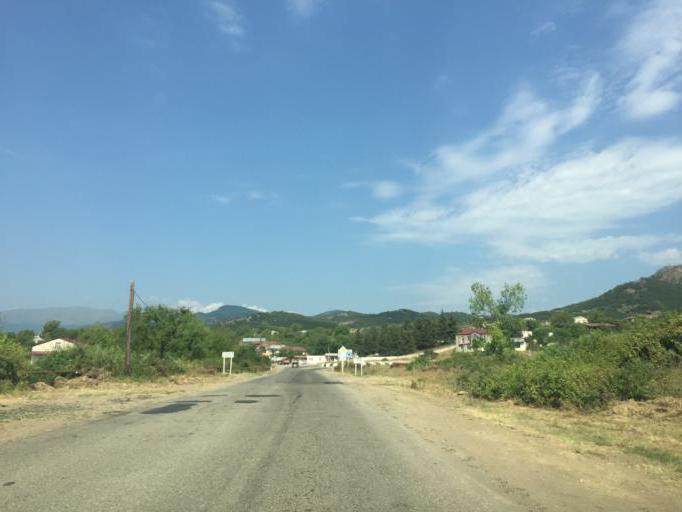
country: AZ
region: Xankandi Sahari
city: Xankandi
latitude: 39.8719
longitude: 46.7324
